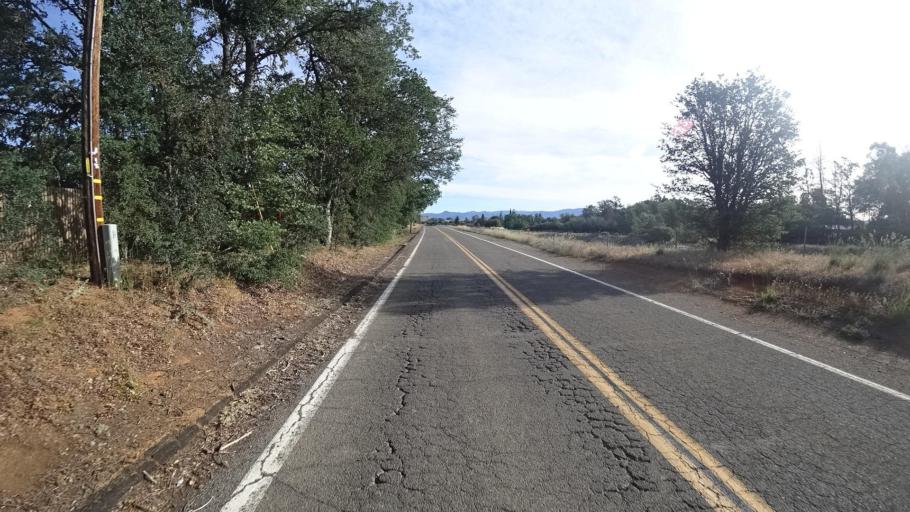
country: US
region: California
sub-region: Lake County
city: Lakeport
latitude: 39.0673
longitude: -122.9323
